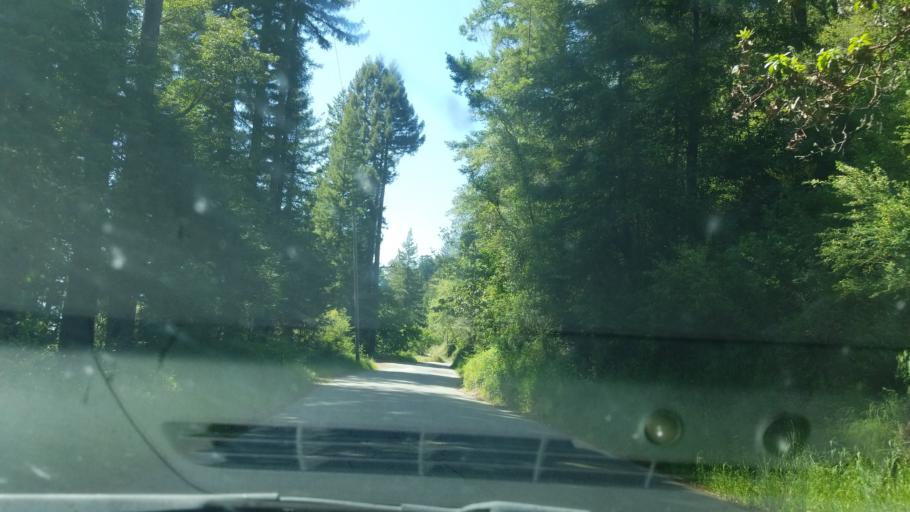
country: US
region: California
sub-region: Santa Cruz County
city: Day Valley
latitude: 37.0855
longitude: -121.8587
